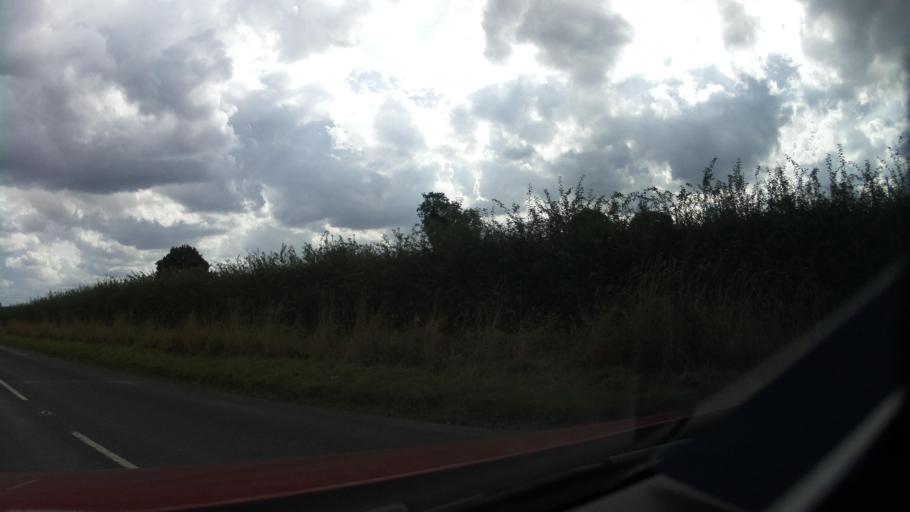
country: GB
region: England
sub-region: North Yorkshire
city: Ripon
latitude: 54.1697
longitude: -1.5512
